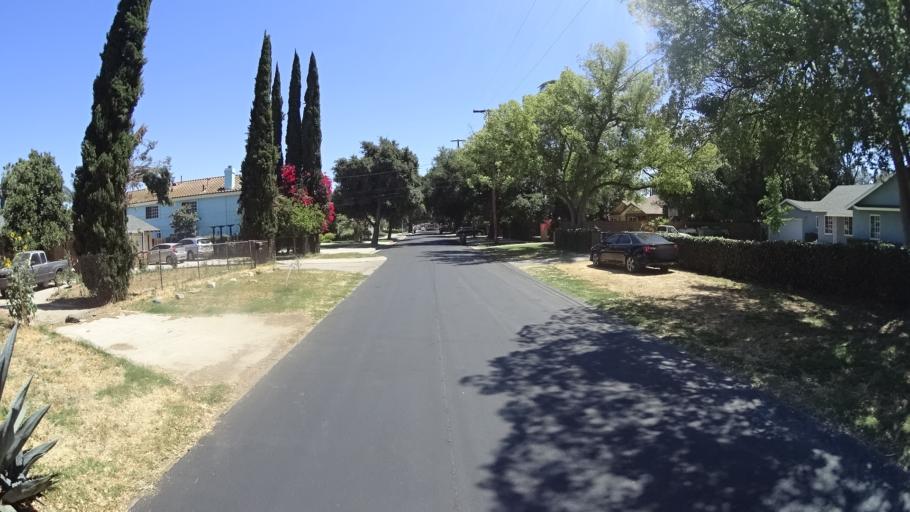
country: US
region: California
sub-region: Los Angeles County
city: Northridge
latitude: 34.1910
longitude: -118.5120
